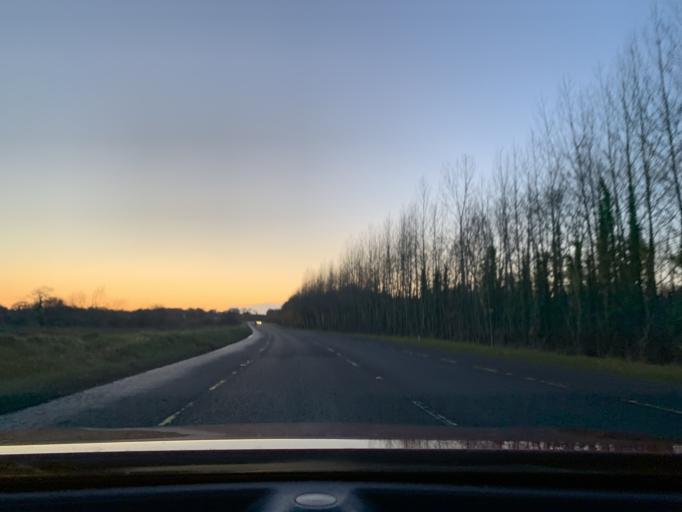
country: IE
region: Connaught
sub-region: County Leitrim
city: Carrick-on-Shannon
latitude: 53.9363
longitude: -8.0275
